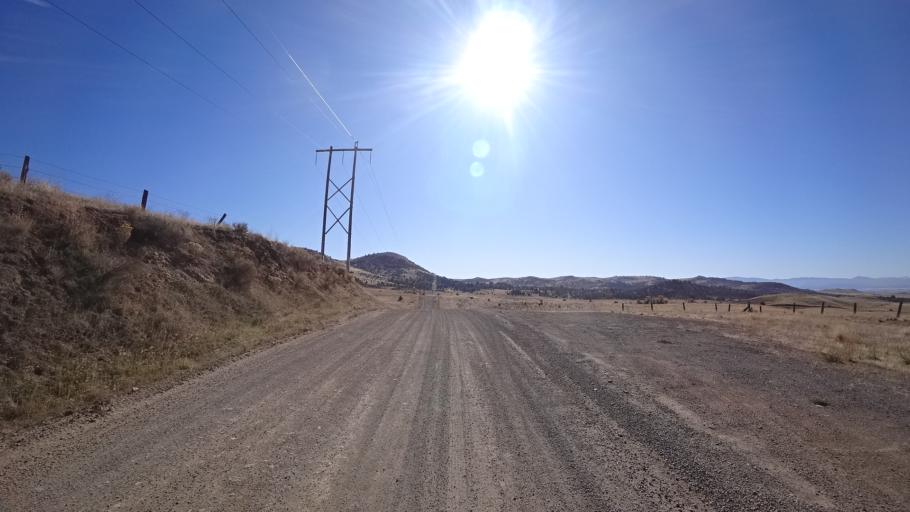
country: US
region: California
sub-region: Siskiyou County
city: Montague
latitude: 41.8186
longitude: -122.3620
